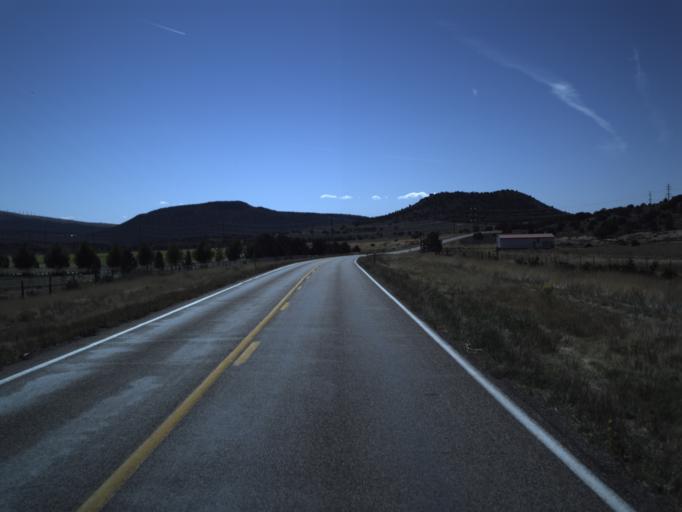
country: US
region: Utah
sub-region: Washington County
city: Enterprise
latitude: 37.4132
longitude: -113.6329
